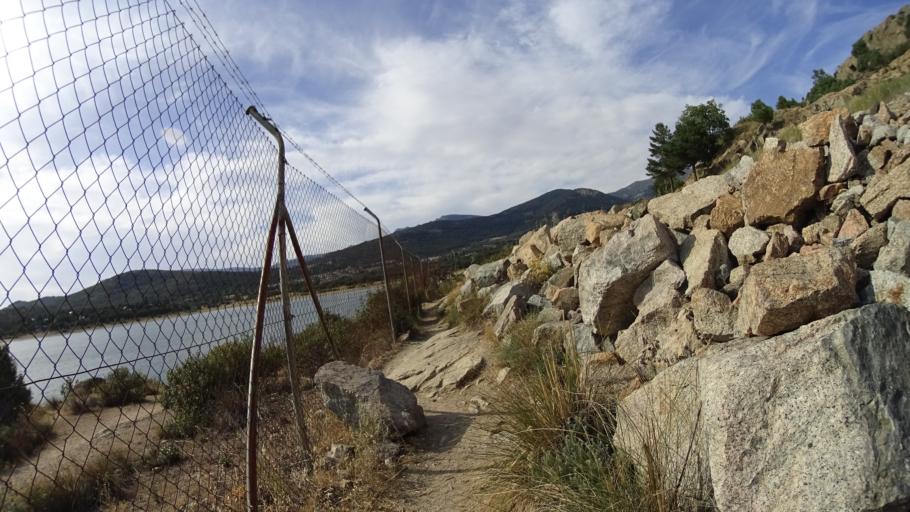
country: ES
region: Madrid
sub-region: Provincia de Madrid
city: Becerril de la Sierra
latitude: 40.7173
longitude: -4.0038
